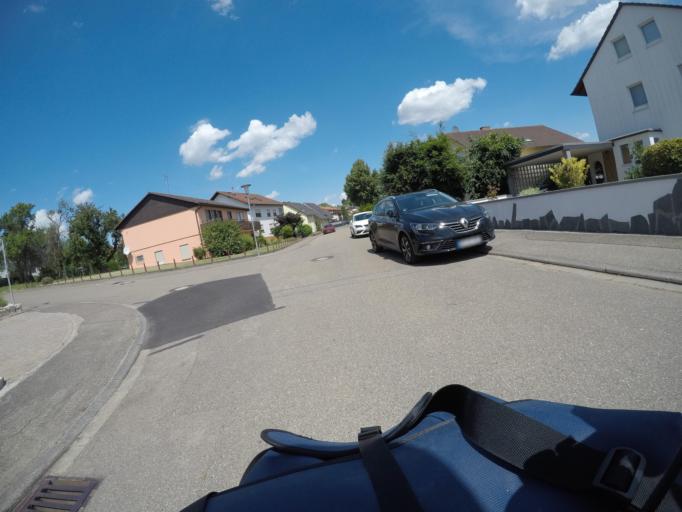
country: DE
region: Baden-Wuerttemberg
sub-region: Karlsruhe Region
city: Sinsheim
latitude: 49.2069
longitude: 8.8771
